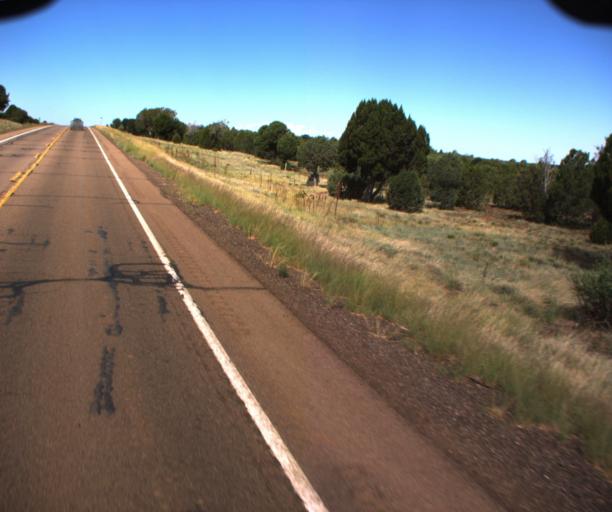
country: US
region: Arizona
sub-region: Navajo County
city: White Mountain Lake
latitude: 34.2717
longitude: -109.9187
